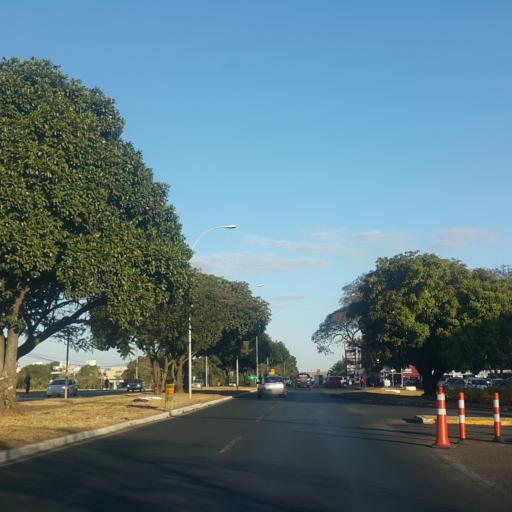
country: BR
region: Federal District
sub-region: Brasilia
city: Brasilia
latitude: -15.8008
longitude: -47.9328
